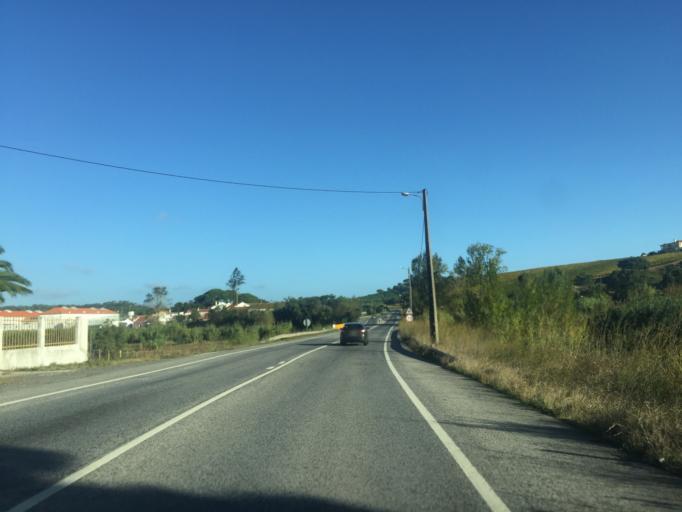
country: PT
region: Lisbon
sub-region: Azambuja
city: Alcoentre
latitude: 39.2085
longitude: -8.9553
